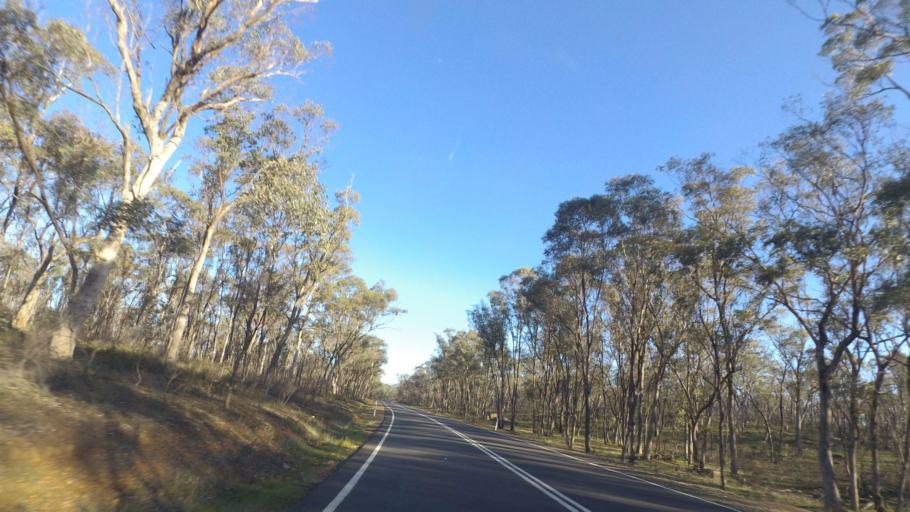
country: AU
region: Victoria
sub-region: Greater Bendigo
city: Kennington
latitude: -36.9183
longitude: 144.4914
